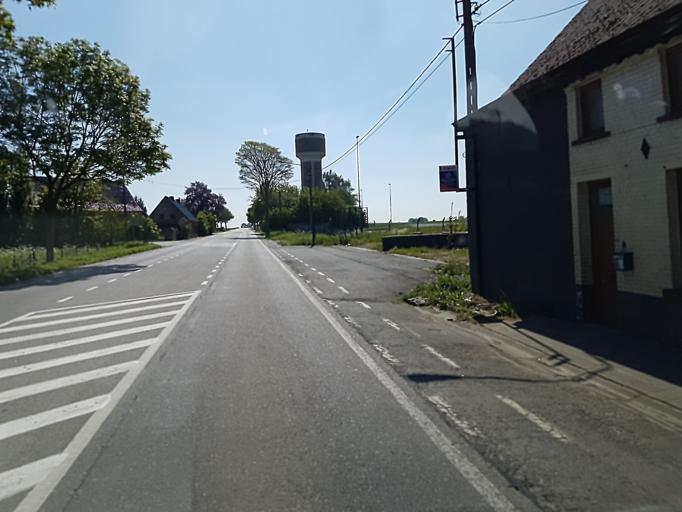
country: BE
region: Wallonia
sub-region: Province du Hainaut
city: Brugelette
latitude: 50.5834
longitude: 3.8522
